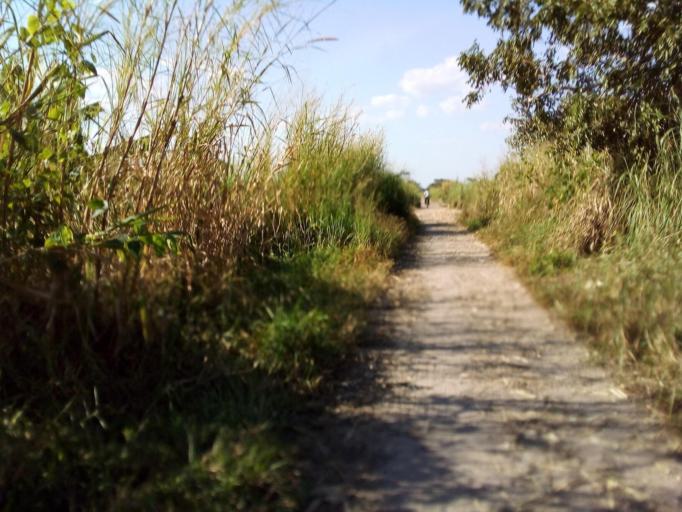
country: MZ
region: Zambezia
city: Quelimane
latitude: -17.5832
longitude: 36.8440
